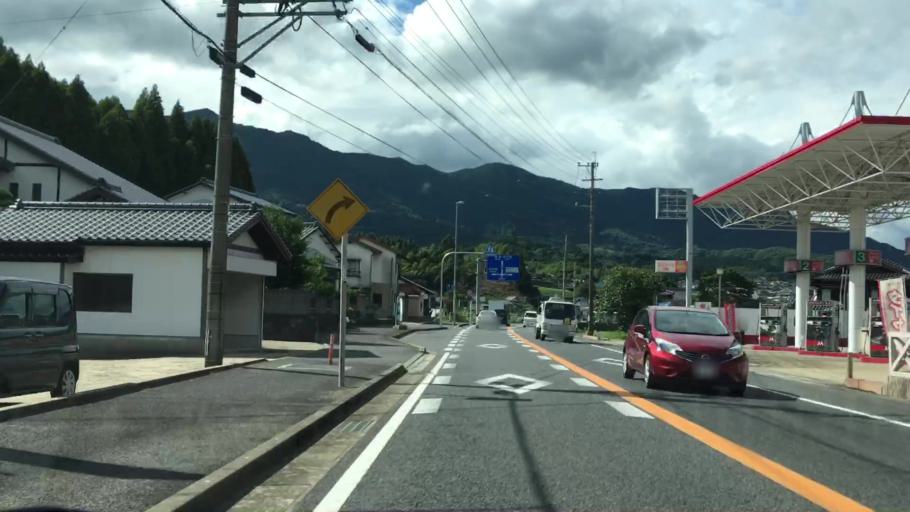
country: JP
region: Saga Prefecture
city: Imaricho-ko
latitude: 33.2226
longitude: 129.8487
